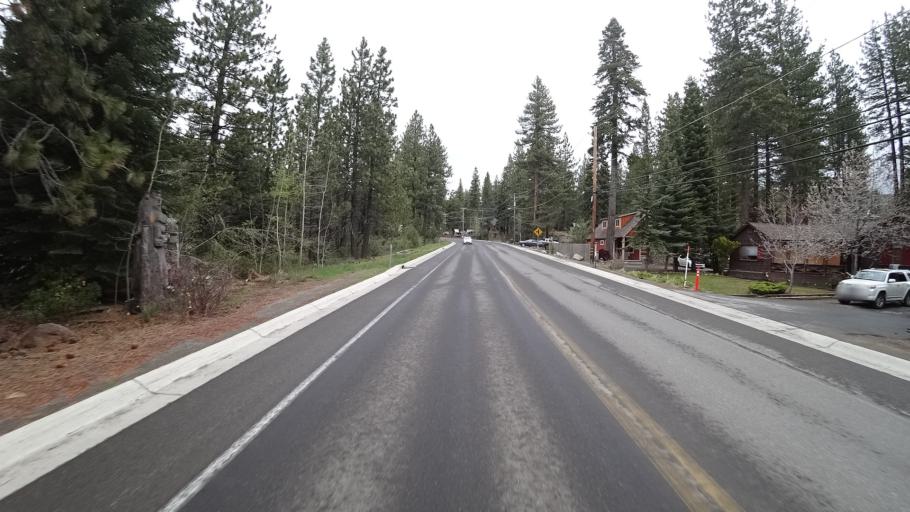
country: US
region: California
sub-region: Placer County
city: Kings Beach
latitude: 39.2446
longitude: -120.0304
